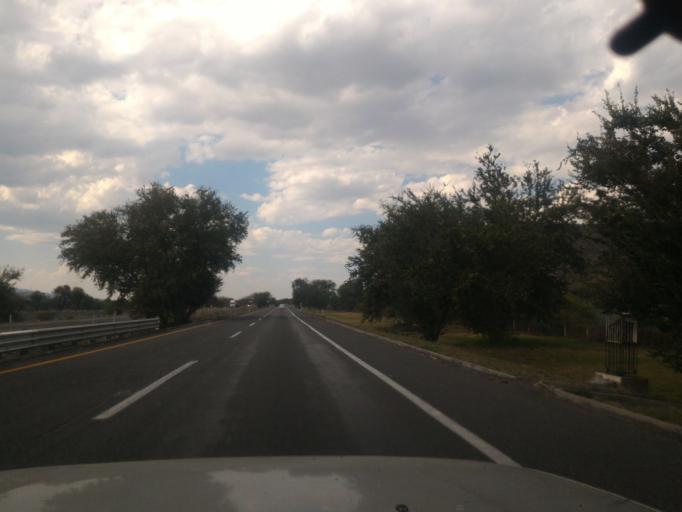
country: MX
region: Jalisco
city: Zacoalco de Torres
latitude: 20.1880
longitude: -103.5178
